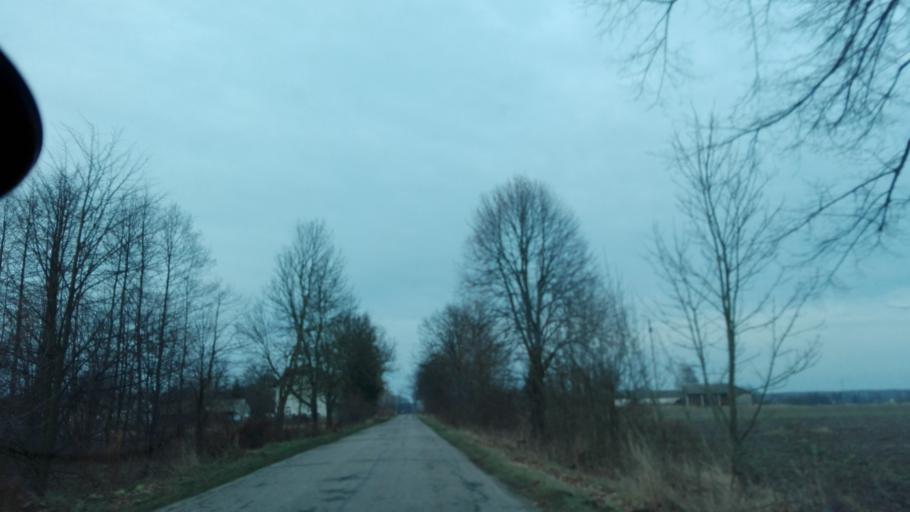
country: PL
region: Lublin Voivodeship
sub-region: Powiat bialski
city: Sosnowka
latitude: 51.7269
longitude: 23.4229
